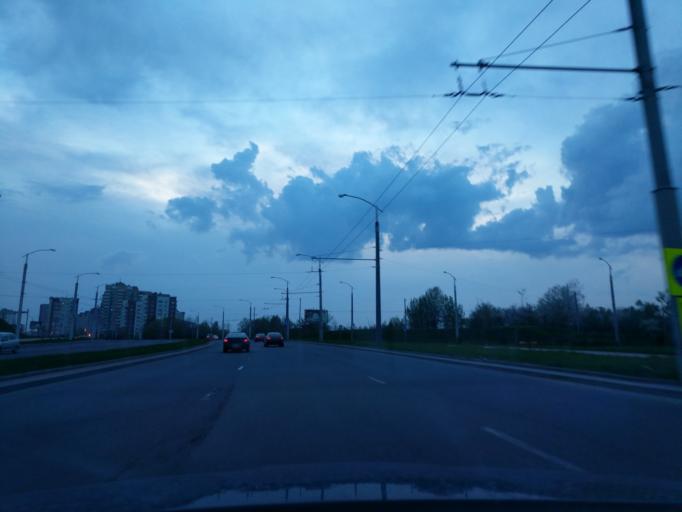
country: BY
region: Minsk
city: Novoye Medvezhino
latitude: 53.8718
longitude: 27.4918
